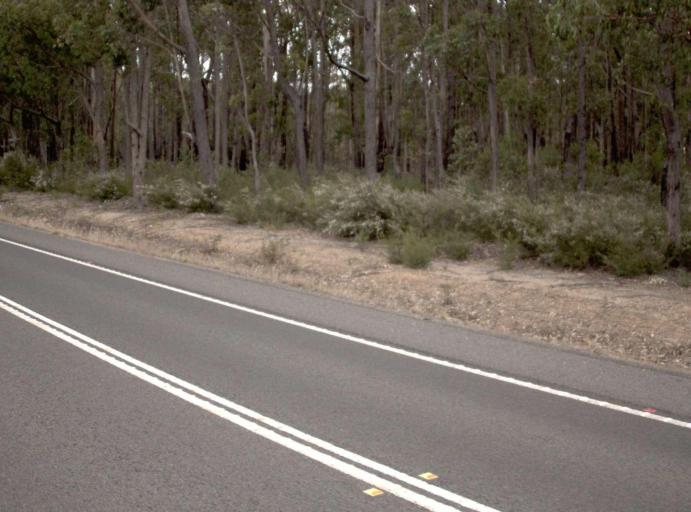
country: AU
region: Victoria
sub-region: East Gippsland
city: Lakes Entrance
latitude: -37.7299
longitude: 147.9453
